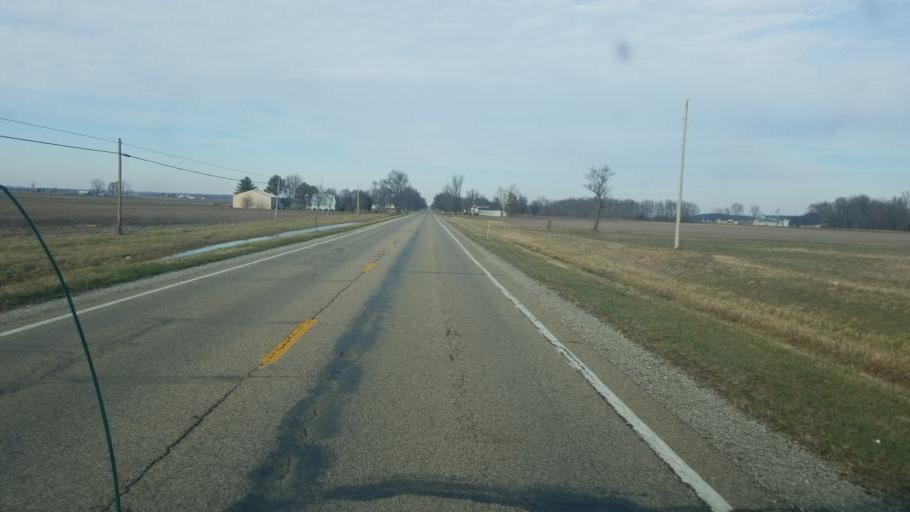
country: US
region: Illinois
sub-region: Lawrence County
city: Bridgeport
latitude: 38.5802
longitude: -87.6945
